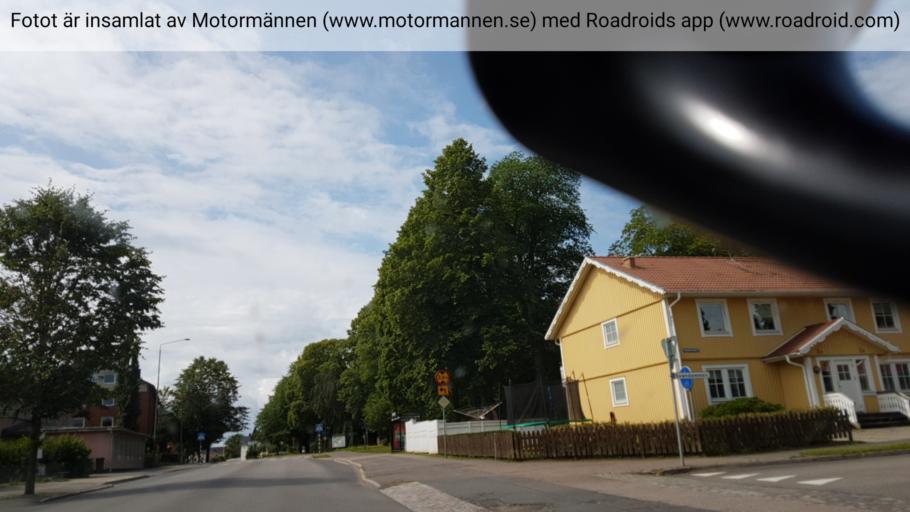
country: SE
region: Vaestra Goetaland
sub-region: Falkopings Kommun
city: Falkoeping
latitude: 58.1812
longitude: 13.5511
